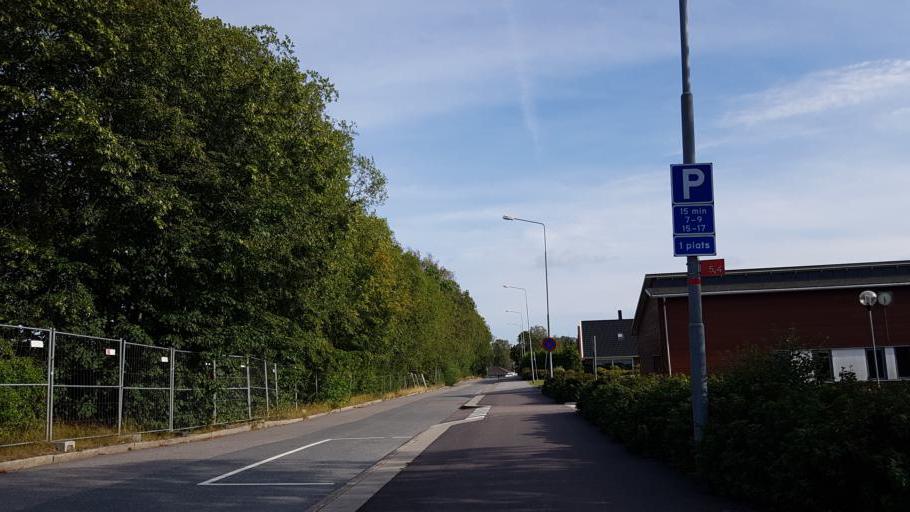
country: SE
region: Vaestra Goetaland
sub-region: Molndal
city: Moelndal
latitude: 57.6646
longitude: 12.0369
